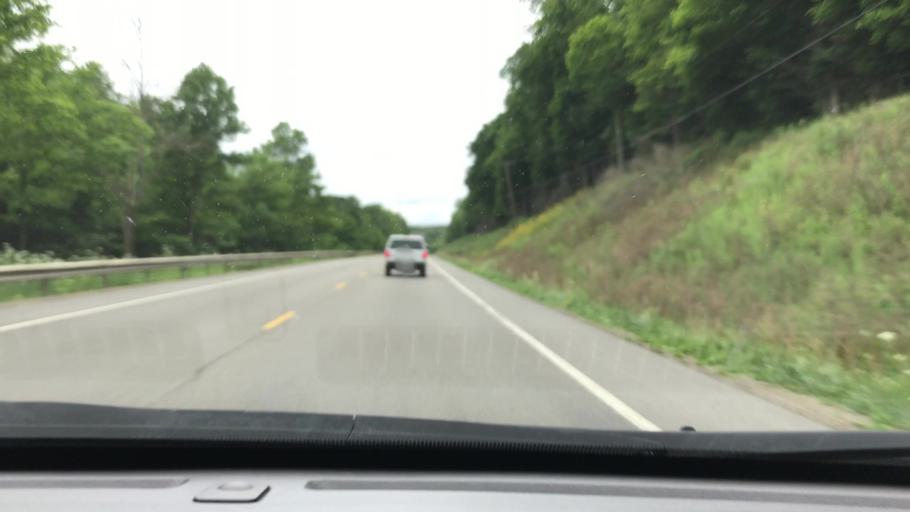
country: US
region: Pennsylvania
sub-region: McKean County
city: Kane
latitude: 41.6889
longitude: -78.6899
